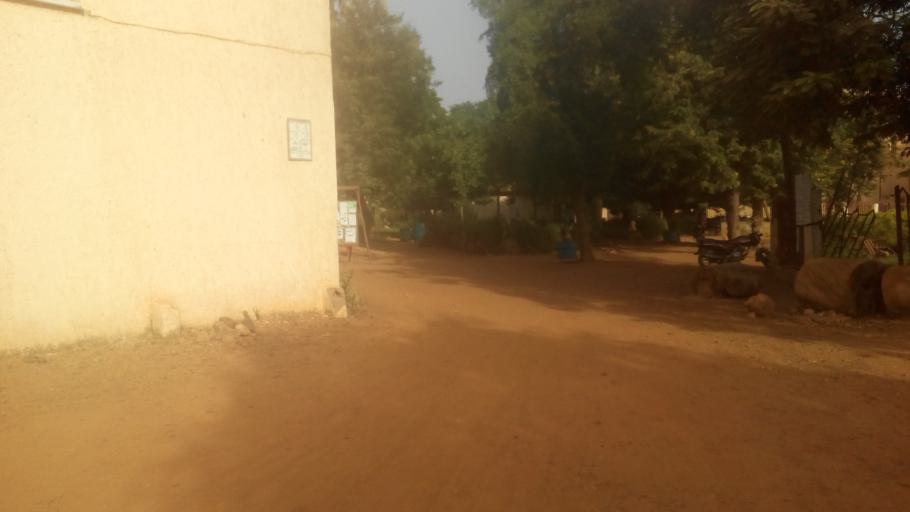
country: NE
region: Niamey
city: Niamey
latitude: 13.5009
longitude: 2.0990
